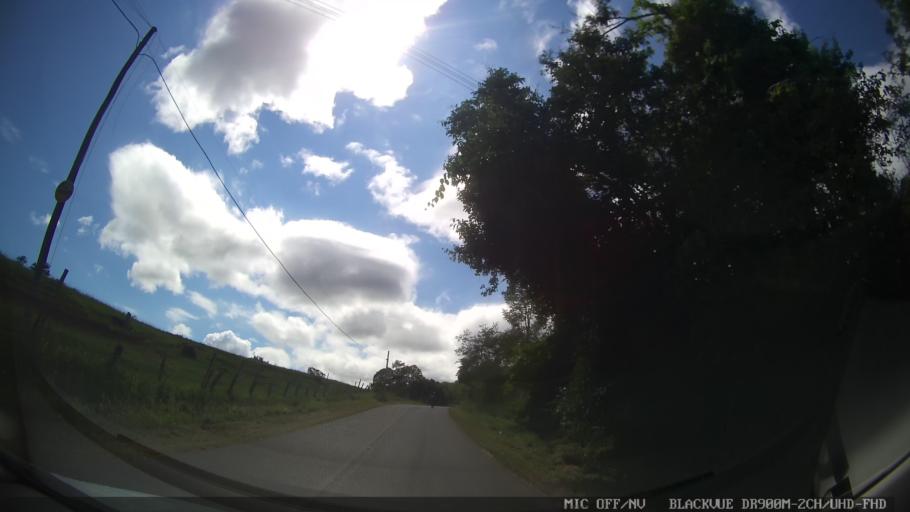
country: BR
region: Sao Paulo
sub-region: Amparo
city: Amparo
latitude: -22.8565
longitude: -46.7701
